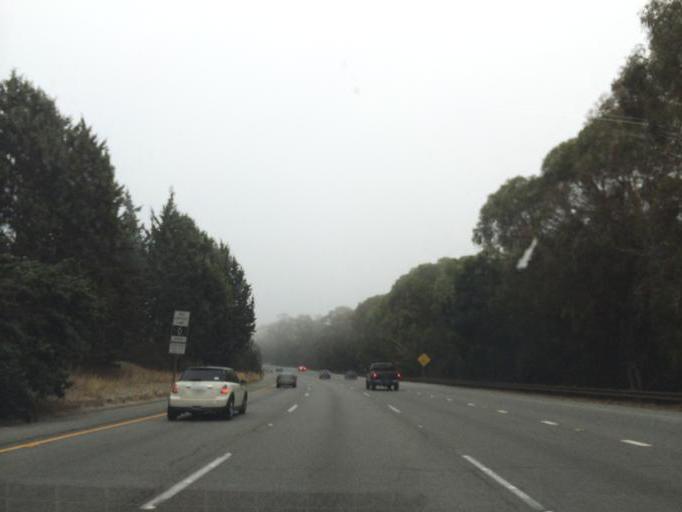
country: US
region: California
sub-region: Santa Clara County
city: Loyola
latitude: 37.3568
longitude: -122.1169
